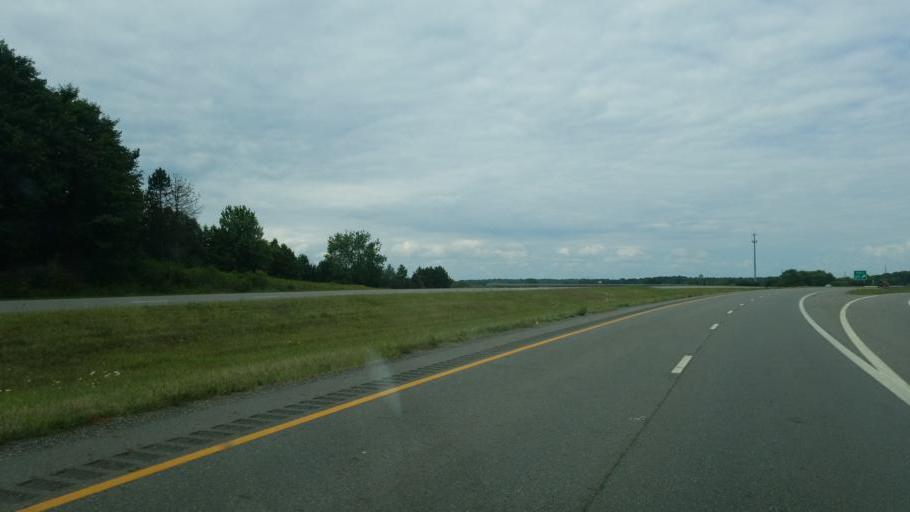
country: US
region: Ohio
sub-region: Columbiana County
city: Columbiana
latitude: 40.9245
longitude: -80.7212
